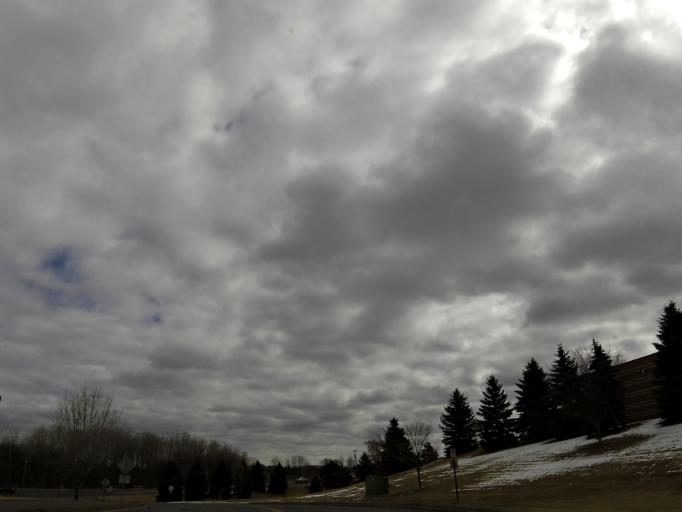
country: US
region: Minnesota
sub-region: Washington County
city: Woodbury
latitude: 44.9284
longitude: -92.9562
